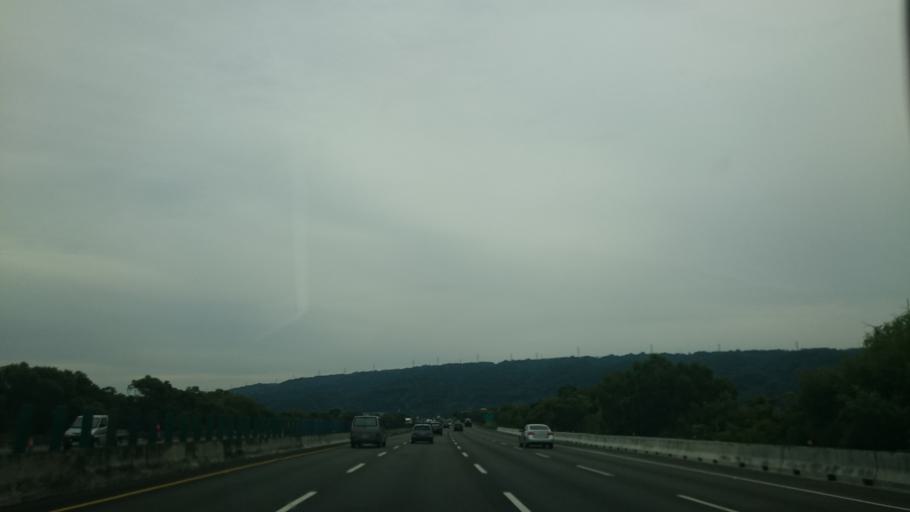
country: TW
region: Taiwan
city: Zhongxing New Village
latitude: 23.9792
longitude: 120.6515
